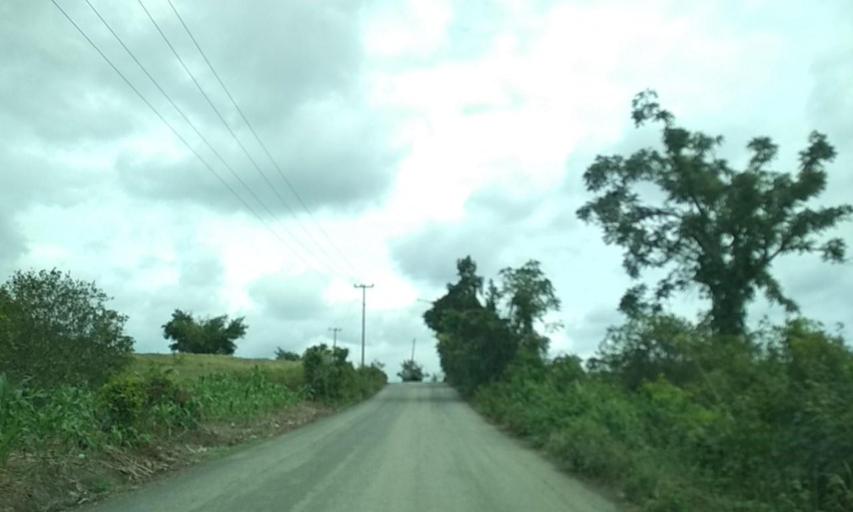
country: MX
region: Veracruz
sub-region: Papantla
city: El Chote
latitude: 20.3553
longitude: -97.3456
